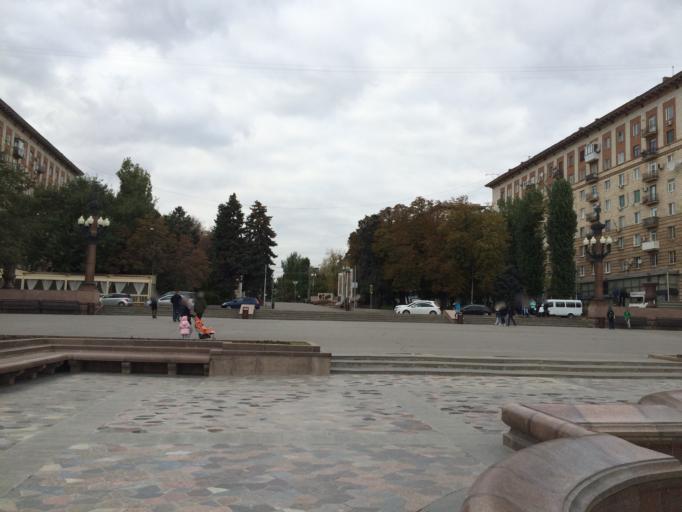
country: RU
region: Volgograd
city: Volgograd
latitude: 48.7045
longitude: 44.5205
